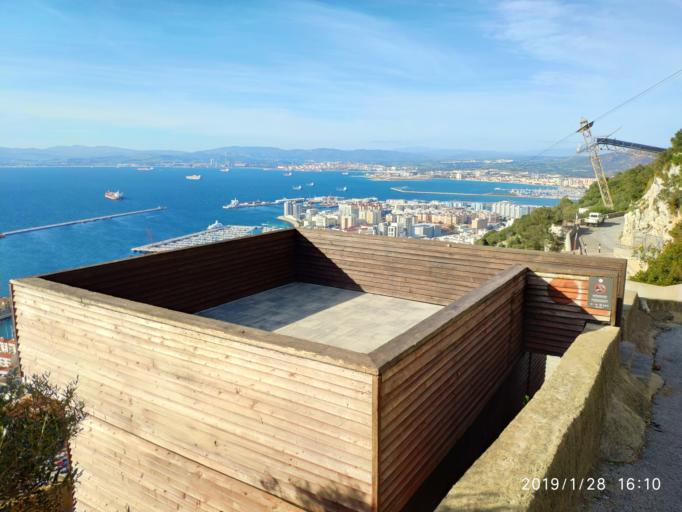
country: GI
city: Gibraltar
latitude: 36.1322
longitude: -5.3486
